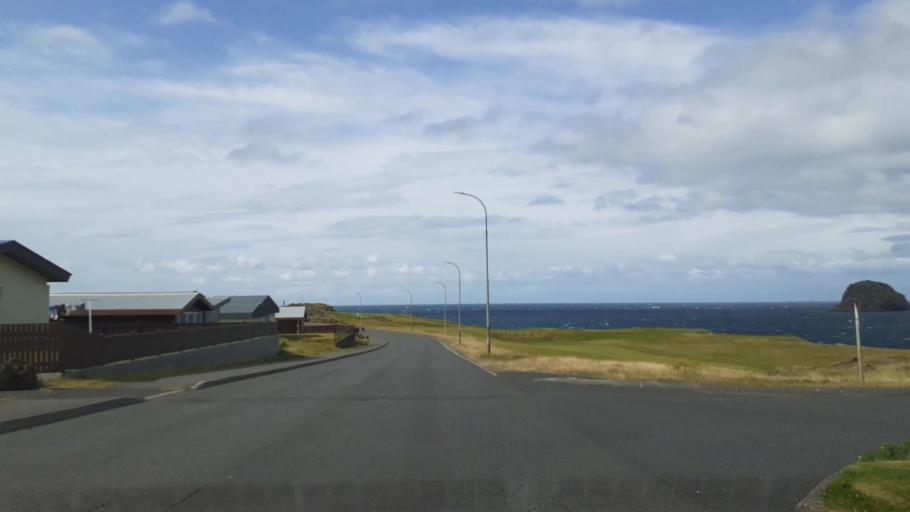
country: IS
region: South
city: Vestmannaeyjar
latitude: 63.4362
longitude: -20.2963
